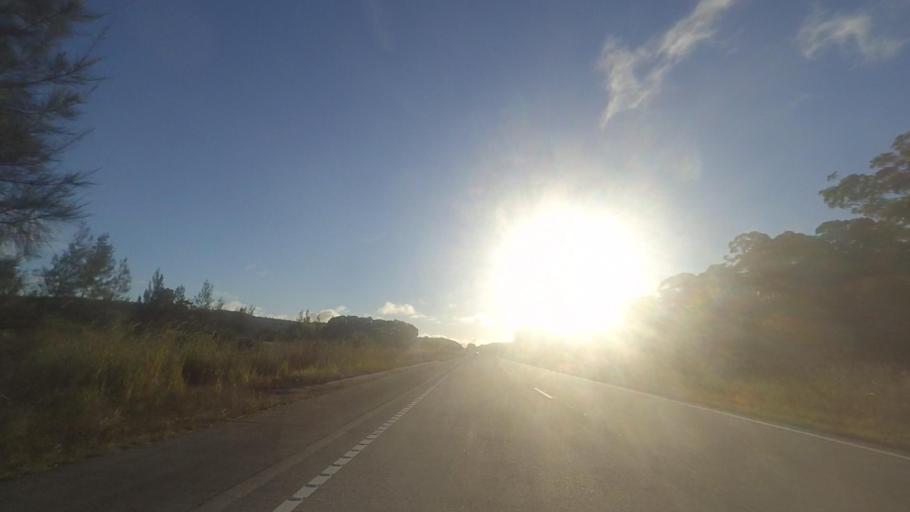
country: AU
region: New South Wales
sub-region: Great Lakes
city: Bulahdelah
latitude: -32.5244
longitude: 152.1972
